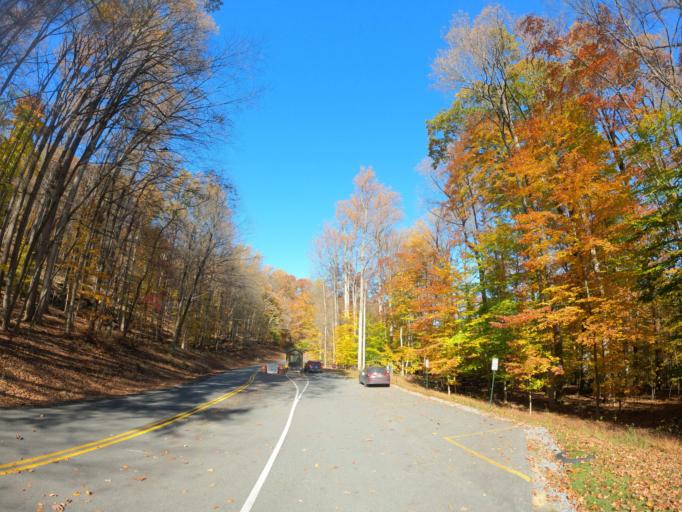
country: US
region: Maryland
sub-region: Frederick County
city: Thurmont
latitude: 39.6244
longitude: -77.4648
